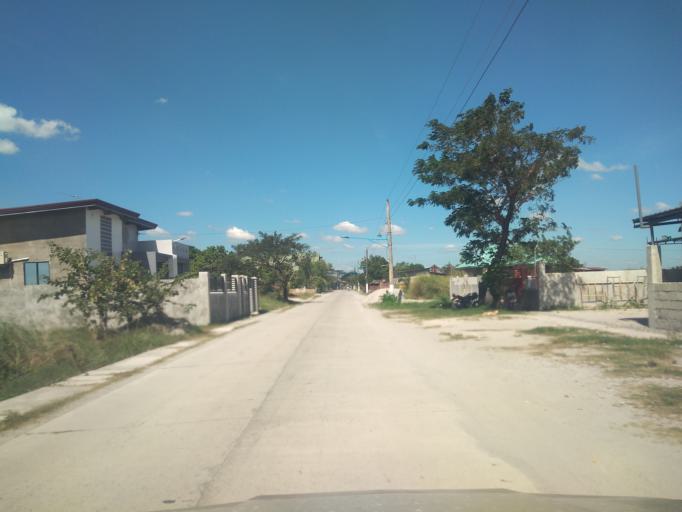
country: PH
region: Central Luzon
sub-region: Province of Pampanga
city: Balas
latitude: 15.0396
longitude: 120.6176
